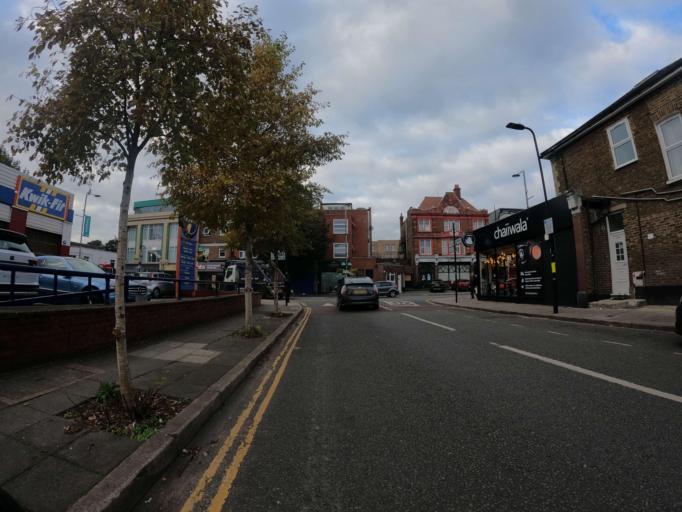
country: GB
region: England
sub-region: Greater London
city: Ealing
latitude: 51.5094
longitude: -0.3276
